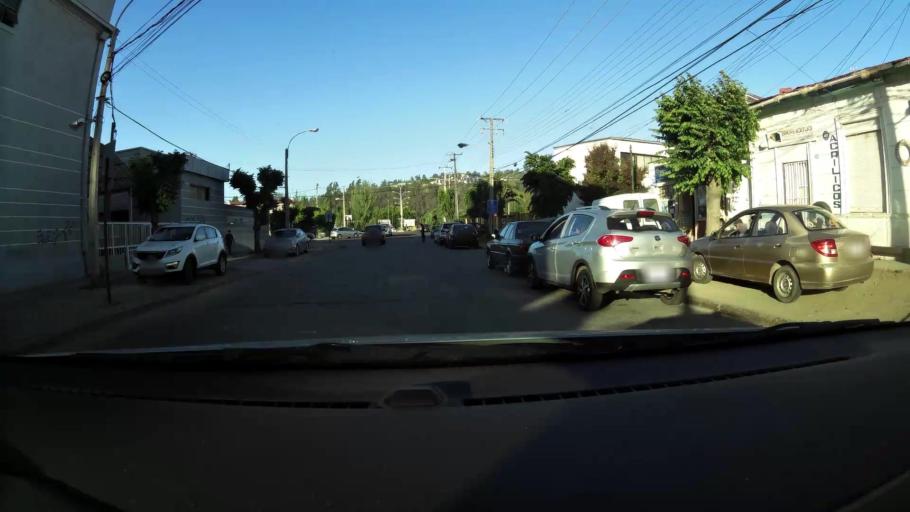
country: CL
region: Valparaiso
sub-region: Provincia de Valparaiso
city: Vina del Mar
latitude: -33.0273
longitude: -71.5400
